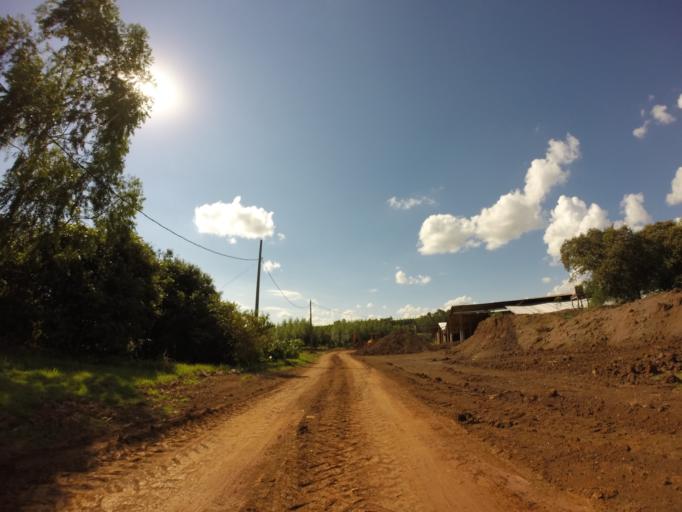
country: PY
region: Alto Parana
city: Ciudad del Este
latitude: -25.3685
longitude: -54.6549
